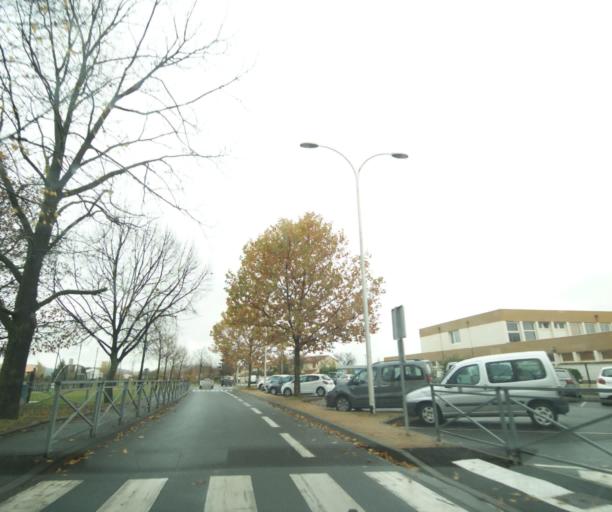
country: FR
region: Auvergne
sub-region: Departement du Puy-de-Dome
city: Cournon-d'Auvergne
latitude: 45.7311
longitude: 3.2014
